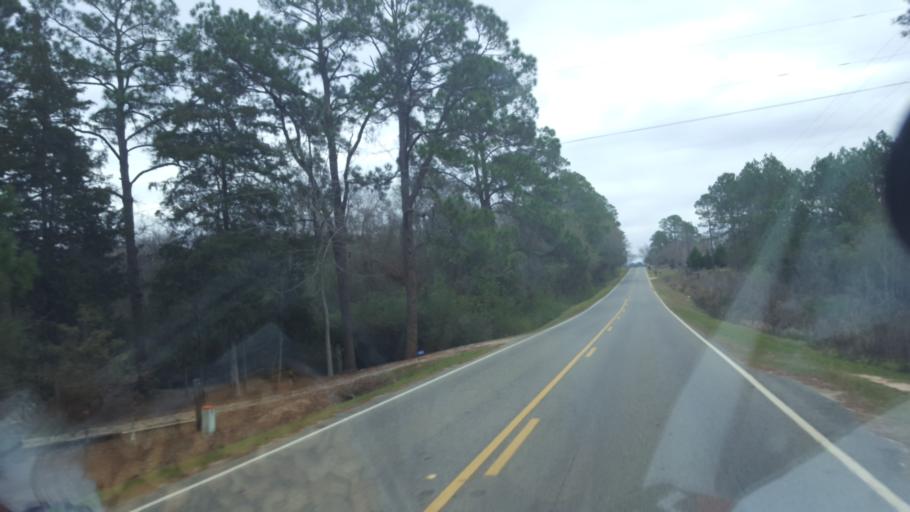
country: US
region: Georgia
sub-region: Ben Hill County
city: Fitzgerald
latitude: 31.7436
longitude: -83.2723
